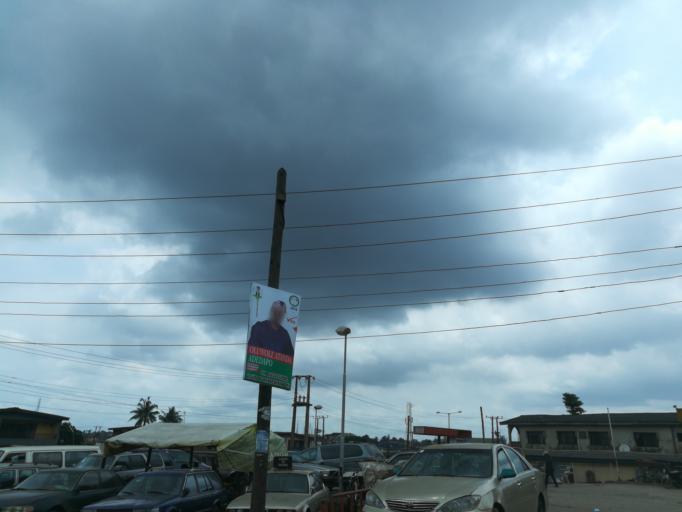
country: NG
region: Lagos
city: Agege
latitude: 6.6147
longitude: 3.3278
